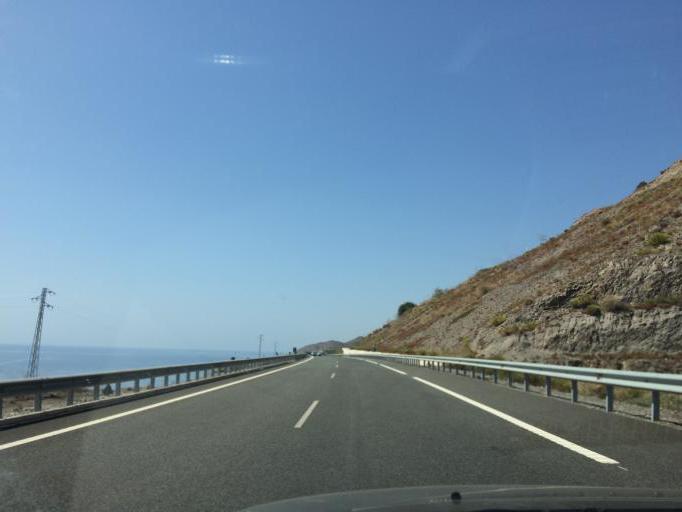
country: ES
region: Andalusia
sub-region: Provincia de Granada
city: Sorvilan
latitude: 36.7571
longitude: -3.2569
